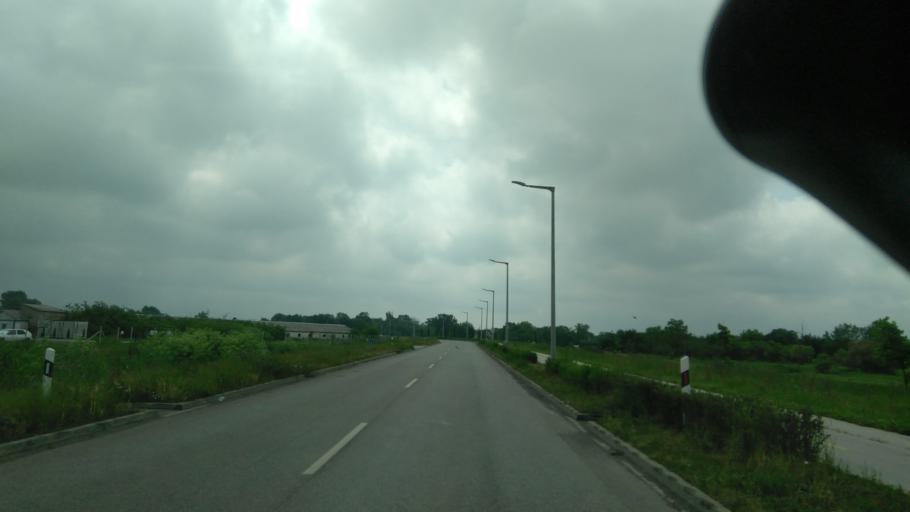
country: HU
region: Bekes
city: Bekescsaba
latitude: 46.6546
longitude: 21.0880
